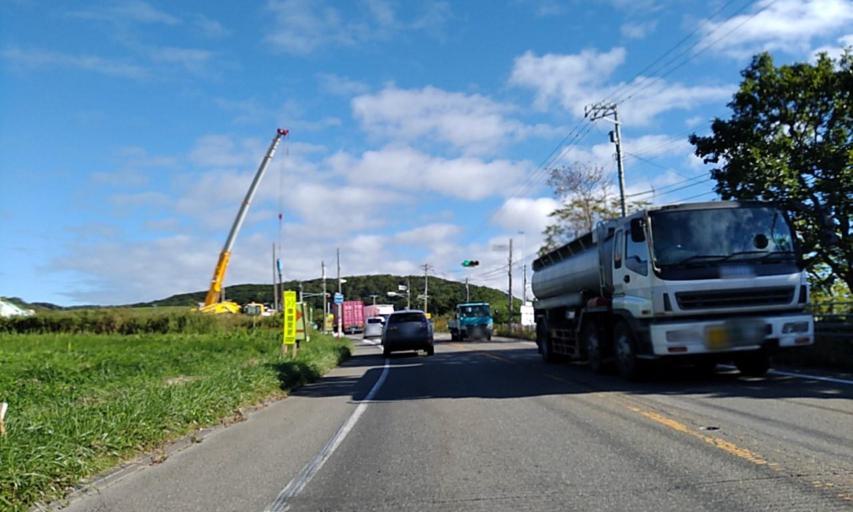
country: JP
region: Hokkaido
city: Shizunai-furukawacho
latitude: 42.3724
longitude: 142.3089
